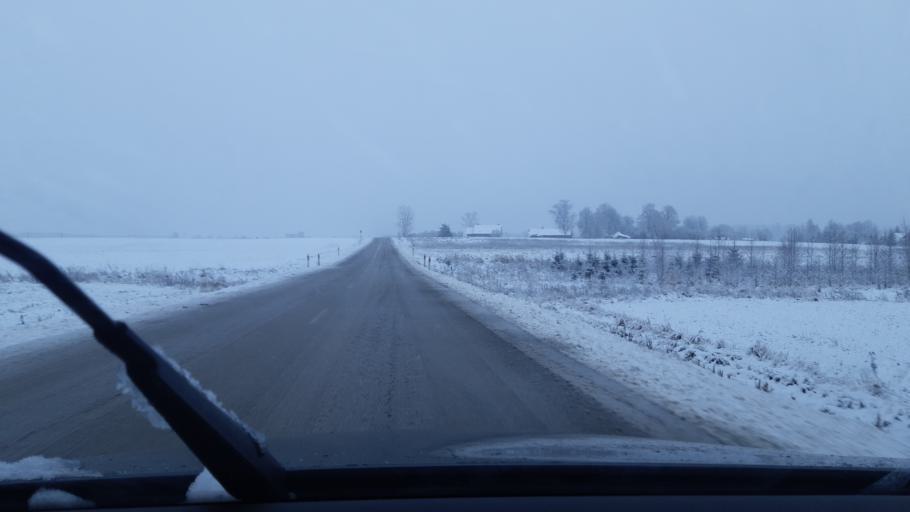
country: LT
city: Kaisiadorys
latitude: 54.8545
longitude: 24.3637
